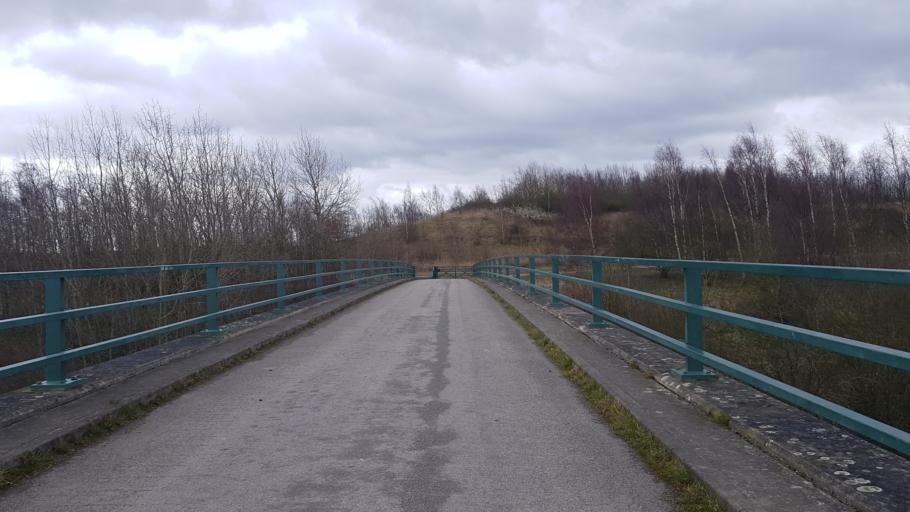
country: GB
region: England
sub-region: City and Borough of Leeds
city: Swillington
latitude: 53.7444
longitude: -1.3993
